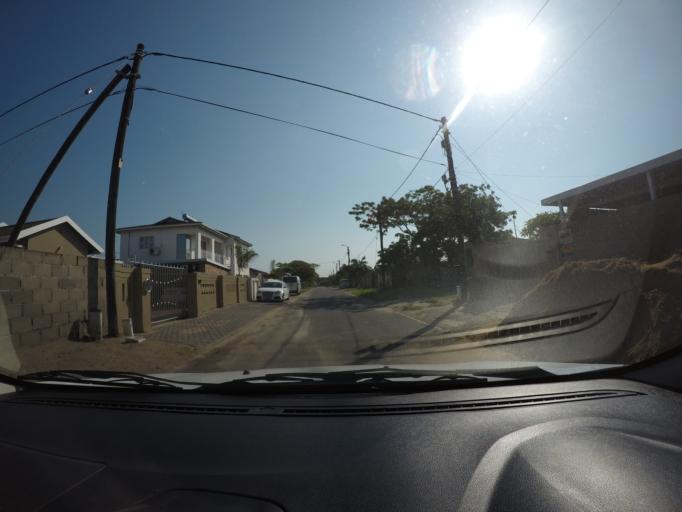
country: ZA
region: KwaZulu-Natal
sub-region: uThungulu District Municipality
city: Richards Bay
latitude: -28.7199
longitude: 32.0370
